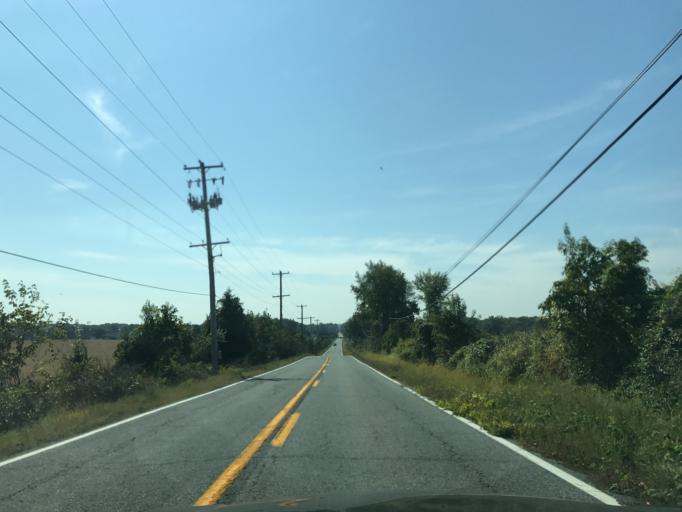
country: US
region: Maryland
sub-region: Cecil County
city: Perryville
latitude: 39.5686
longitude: -76.0530
